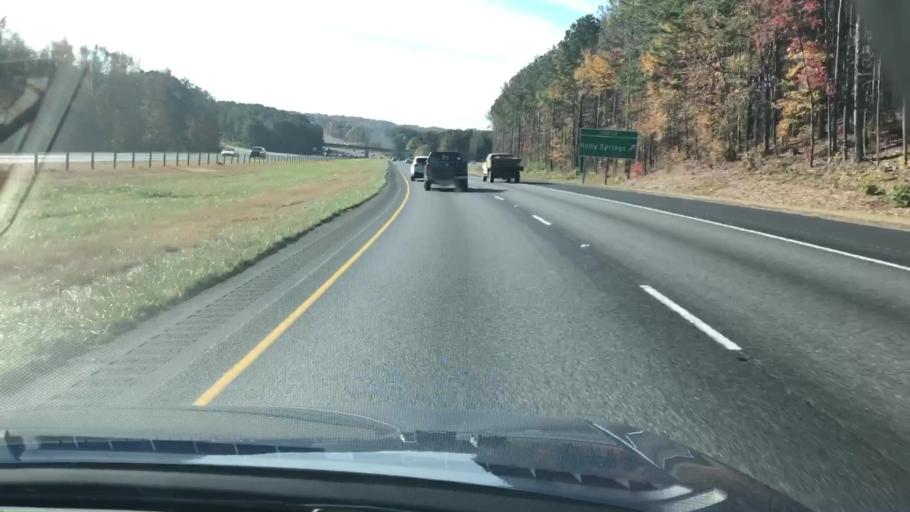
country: US
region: Georgia
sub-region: Cherokee County
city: Holly Springs
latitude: 34.1954
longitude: -84.5037
